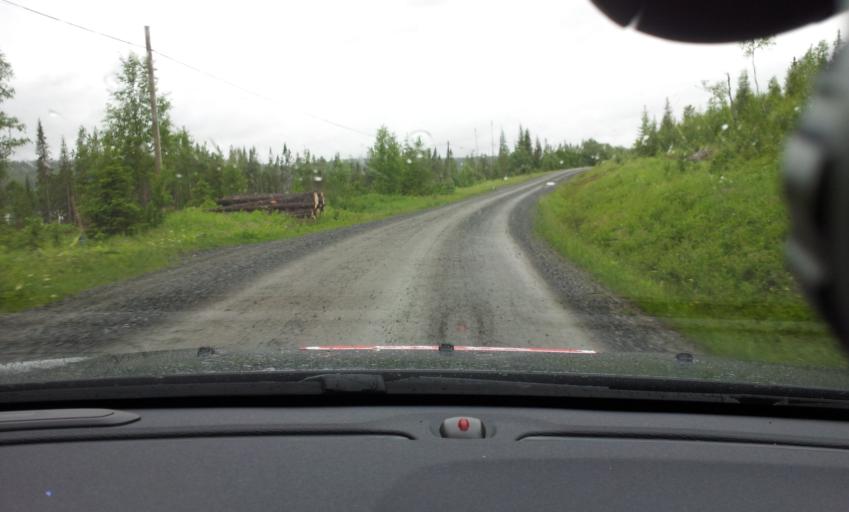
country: SE
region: Jaemtland
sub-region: Are Kommun
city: Are
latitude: 63.4859
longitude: 12.7802
